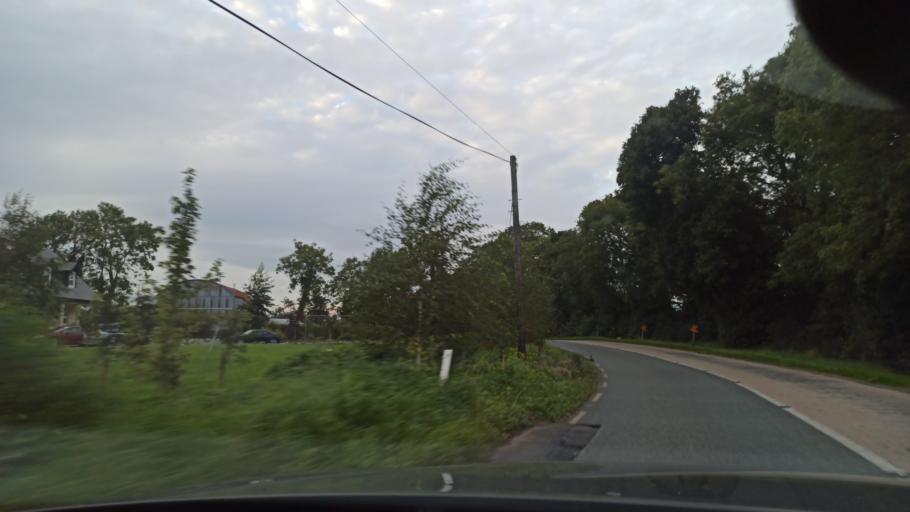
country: IE
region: Munster
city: Cashel
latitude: 52.4832
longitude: -7.8528
